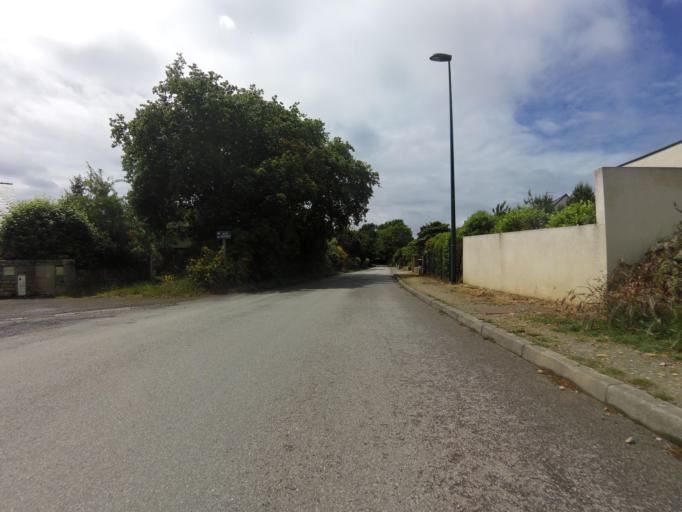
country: FR
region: Brittany
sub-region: Departement du Morbihan
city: Baden
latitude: 47.6127
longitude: -2.9217
